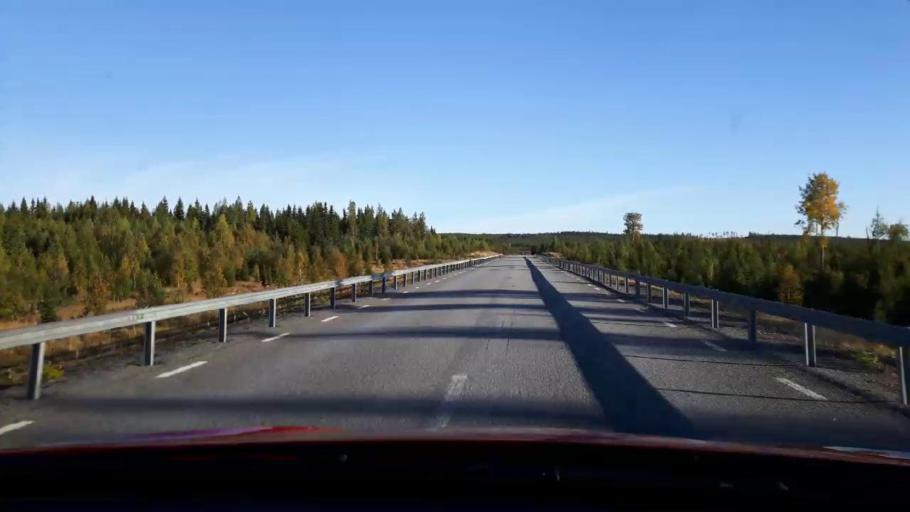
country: SE
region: Jaemtland
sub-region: OEstersunds Kommun
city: Lit
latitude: 63.7741
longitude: 14.7137
